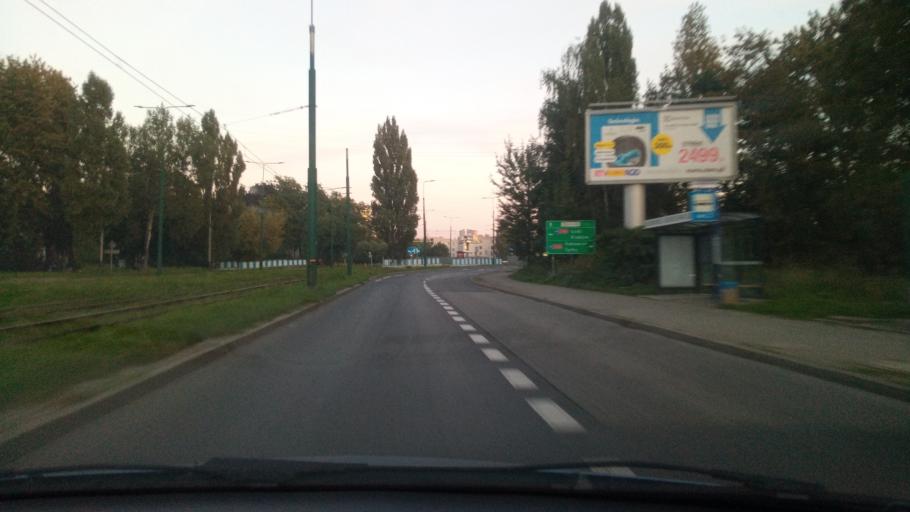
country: PL
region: Silesian Voivodeship
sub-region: Sosnowiec
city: Sosnowiec
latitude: 50.2876
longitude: 19.1016
